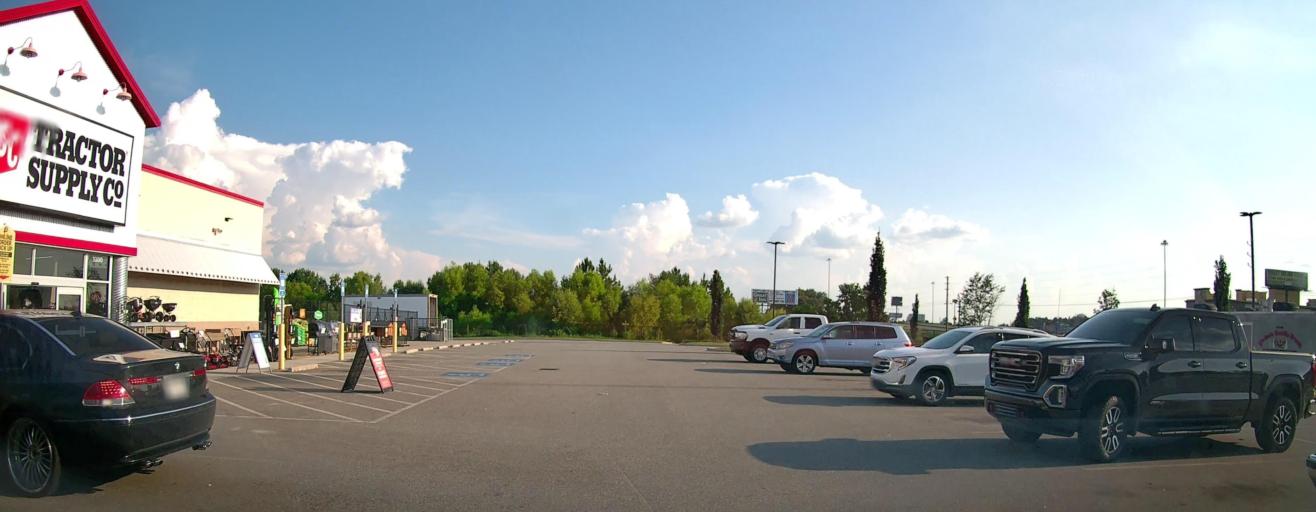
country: US
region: Georgia
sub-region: Houston County
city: Perry
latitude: 32.4756
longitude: -83.7418
